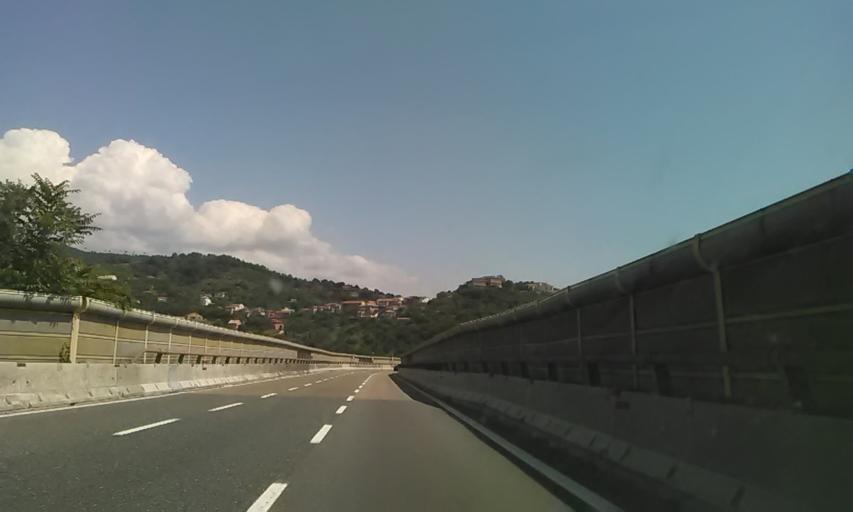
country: IT
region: Liguria
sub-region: Provincia di Savona
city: Celle Ligure
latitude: 44.3461
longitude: 8.5418
